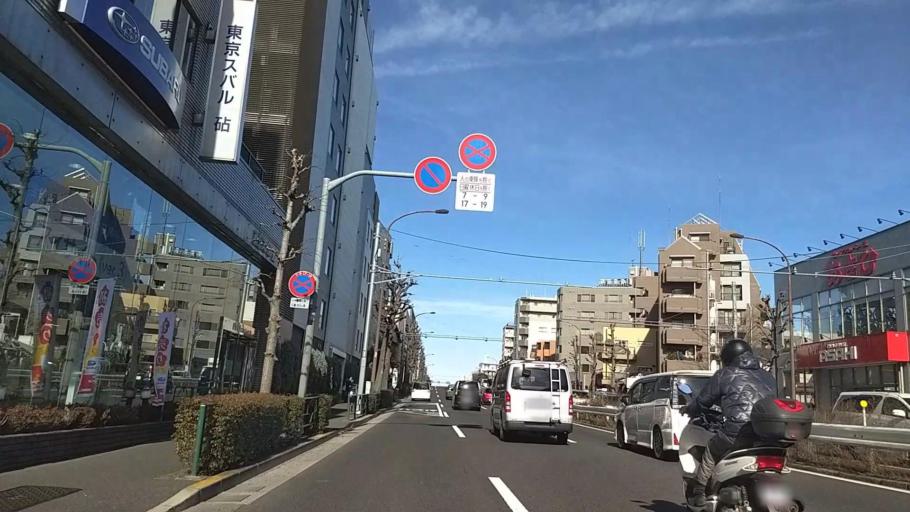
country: JP
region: Tokyo
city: Mitaka-shi
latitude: 35.6422
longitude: 139.6188
